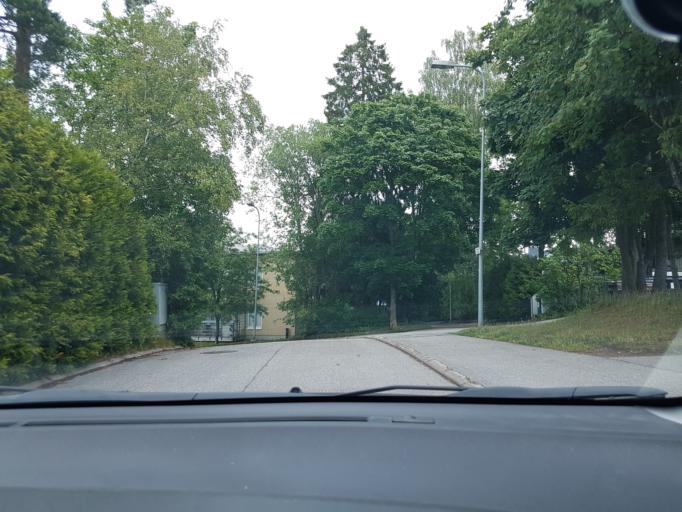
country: FI
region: Uusimaa
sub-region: Helsinki
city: Vantaa
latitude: 60.2682
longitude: 25.0701
